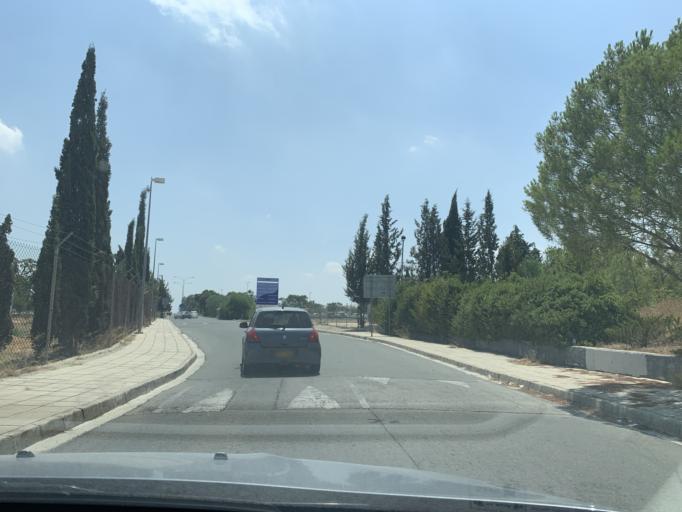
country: CY
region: Lefkosia
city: Tseri
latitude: 35.1141
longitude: 33.3591
